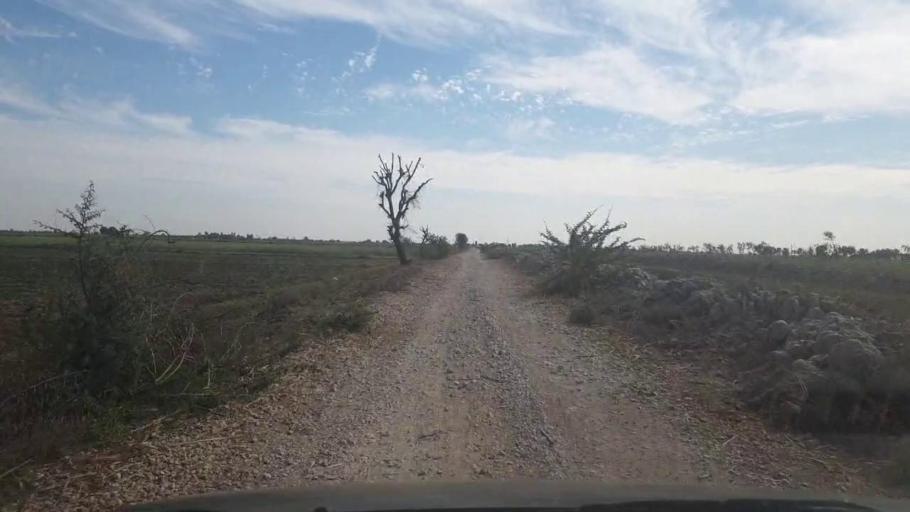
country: PK
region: Sindh
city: Mirwah Gorchani
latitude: 25.4294
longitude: 69.2002
